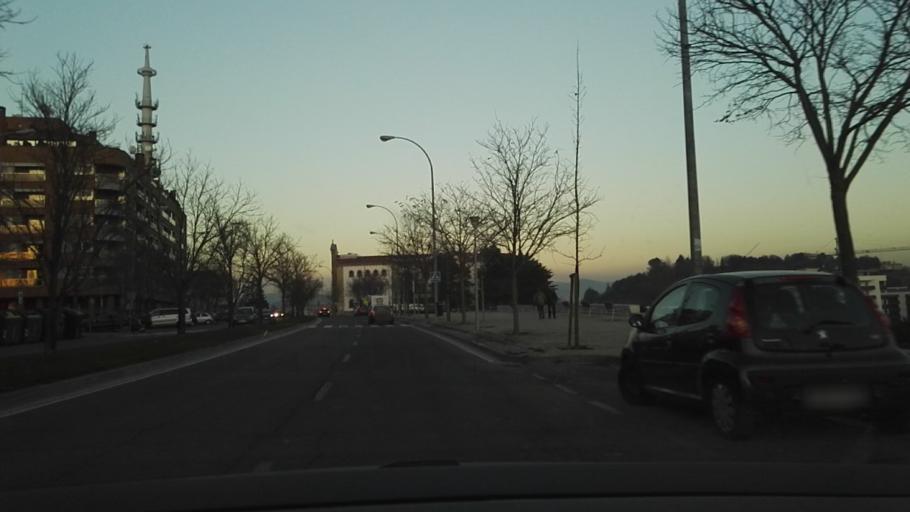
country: ES
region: Navarre
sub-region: Provincia de Navarra
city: Segundo Ensanche
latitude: 42.8087
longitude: -1.6322
